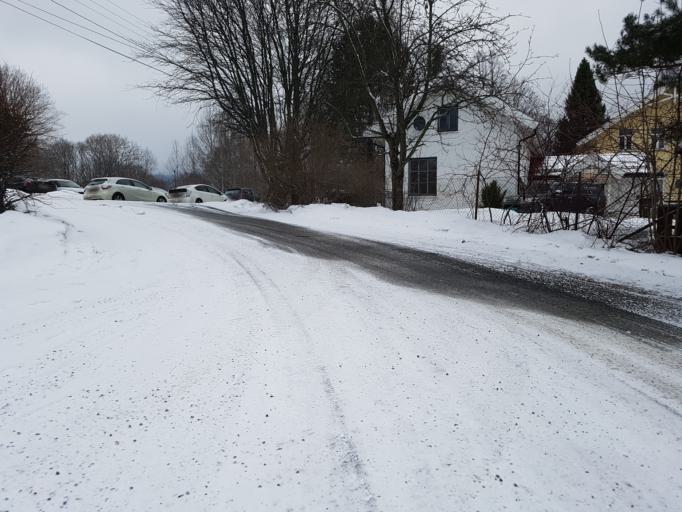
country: NO
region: Buskerud
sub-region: Drammen
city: Drammen
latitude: 59.7412
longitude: 10.1868
